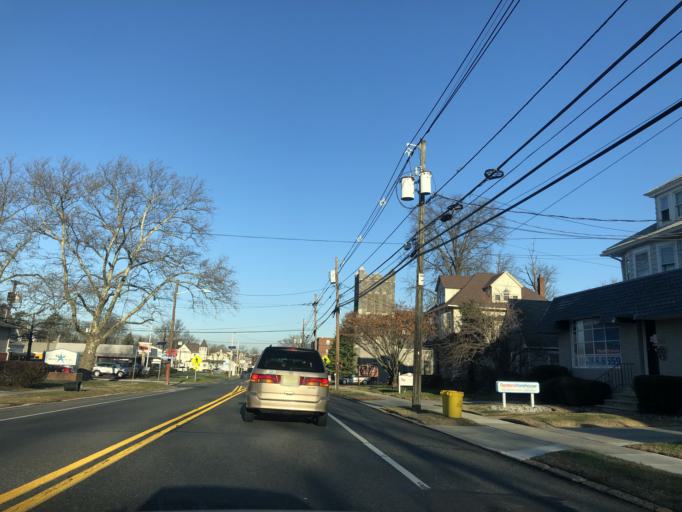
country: US
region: New Jersey
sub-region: Camden County
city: Audubon
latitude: 39.8902
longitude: -75.0644
